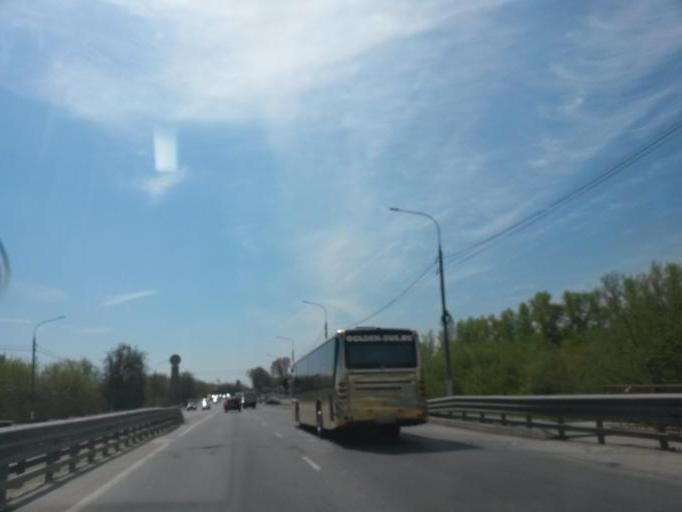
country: RU
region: Moskovskaya
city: Shcherbinka
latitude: 55.4627
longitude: 37.5597
